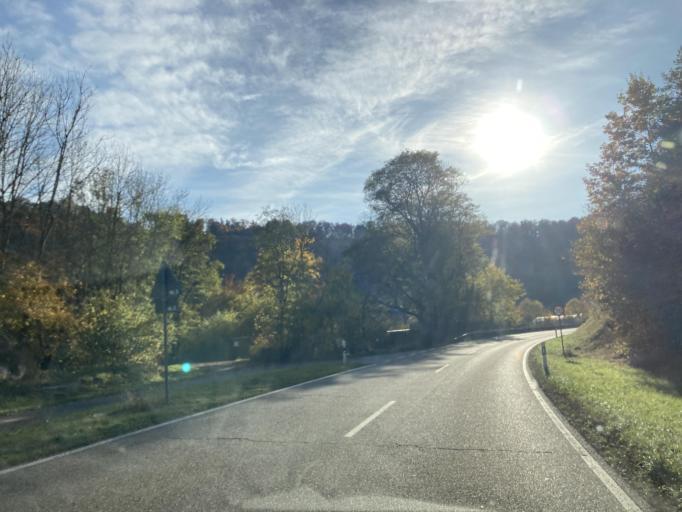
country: DE
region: Baden-Wuerttemberg
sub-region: Karlsruhe Region
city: Horb am Neckar
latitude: 48.4466
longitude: 8.7135
